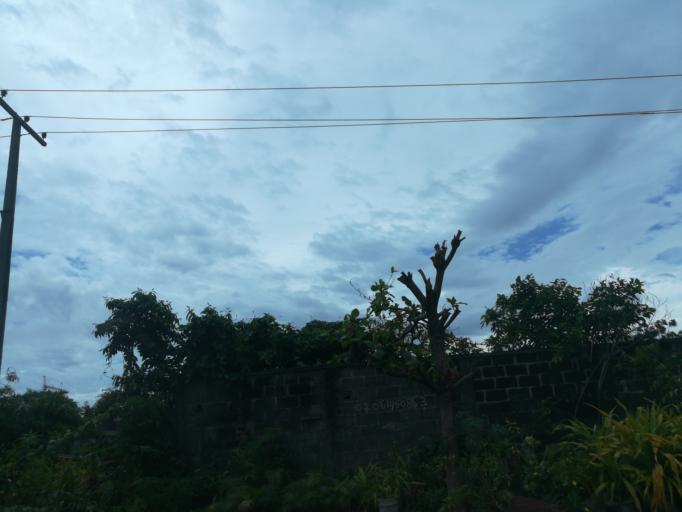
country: NG
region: Lagos
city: Ikoyi
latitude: 6.4399
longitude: 3.4746
